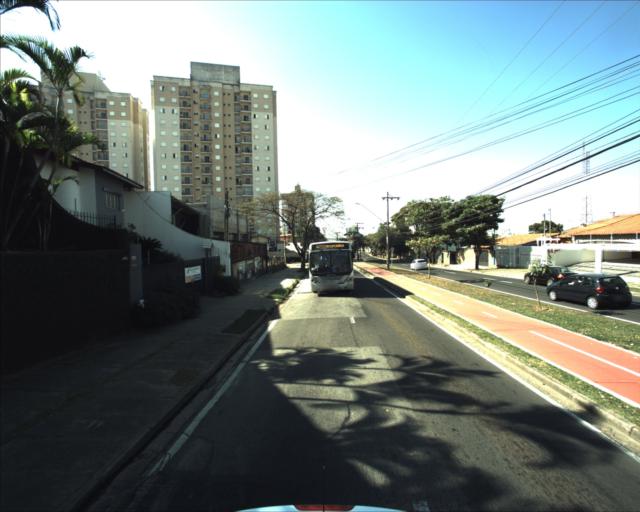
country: BR
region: Sao Paulo
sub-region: Sorocaba
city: Sorocaba
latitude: -23.4891
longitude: -47.4762
